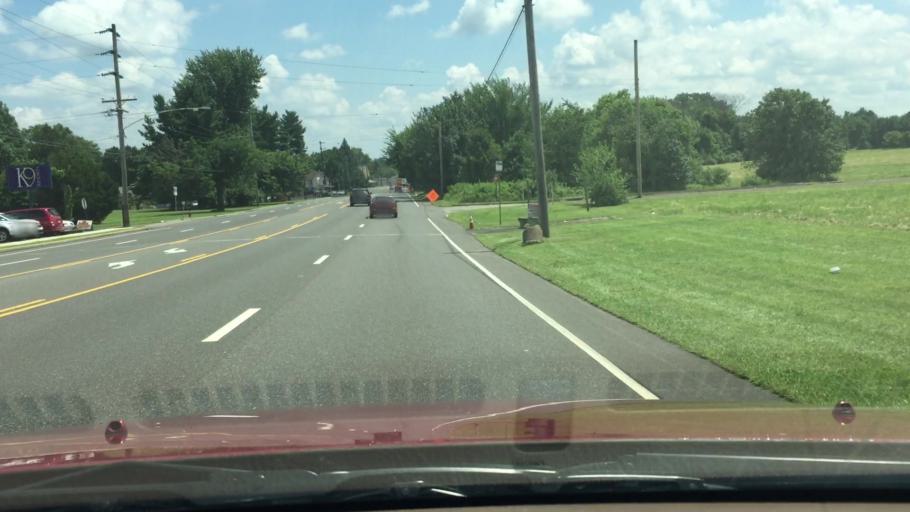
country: US
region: Pennsylvania
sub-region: Montgomery County
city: Horsham
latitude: 40.1874
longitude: -75.1344
